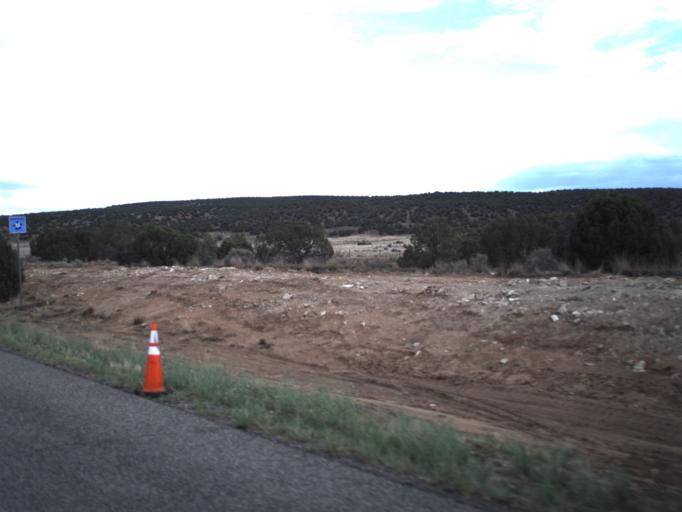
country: US
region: Colorado
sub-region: Mesa County
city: Loma
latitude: 39.1923
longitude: -109.0488
